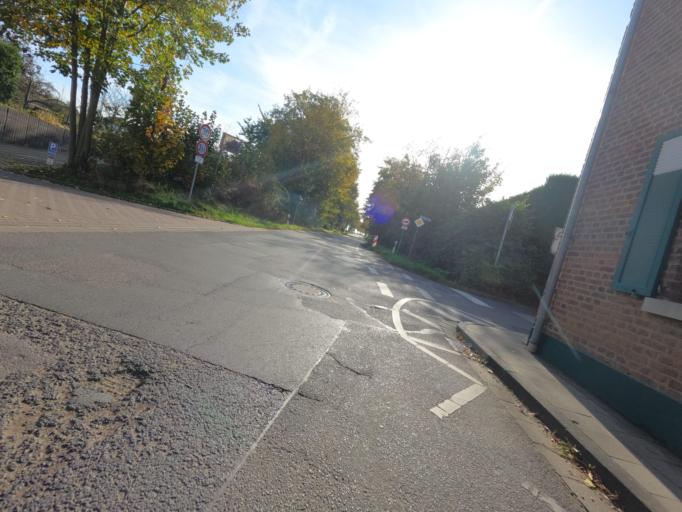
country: DE
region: North Rhine-Westphalia
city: Erkelenz
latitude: 51.0304
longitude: 6.3262
